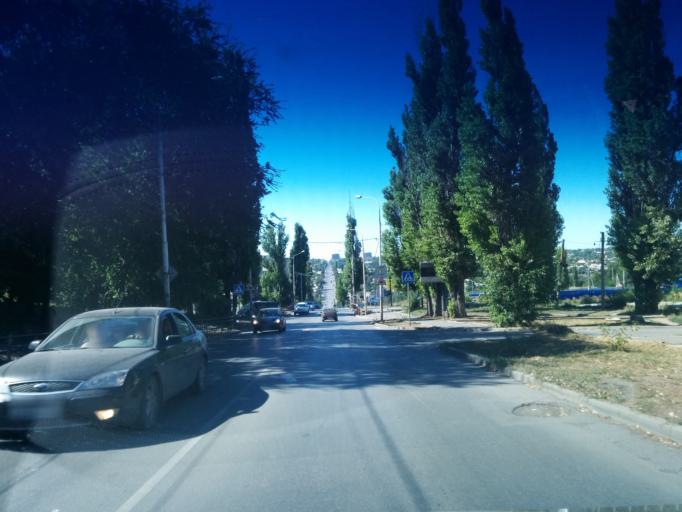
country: RU
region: Rostov
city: Shakhty
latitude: 47.6954
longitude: 40.2433
